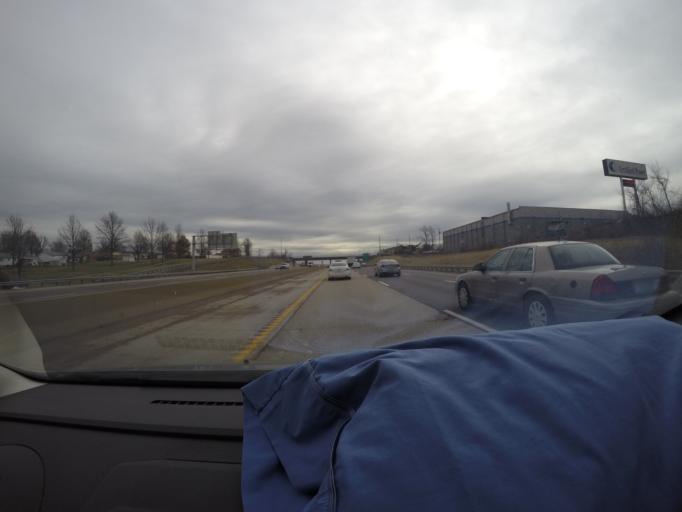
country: US
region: Missouri
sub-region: Saint Louis County
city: Bridgeton
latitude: 38.7441
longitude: -90.4029
